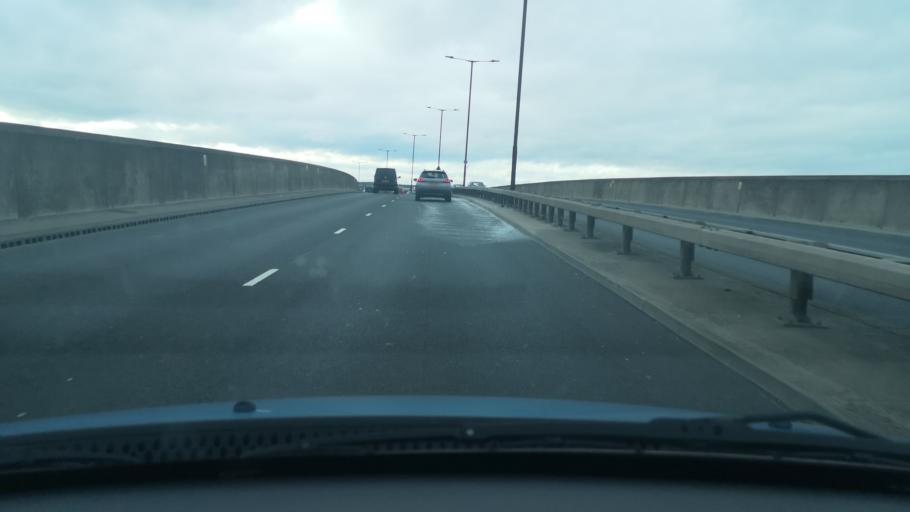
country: GB
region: England
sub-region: Doncaster
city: Doncaster
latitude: 53.5290
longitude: -1.1383
